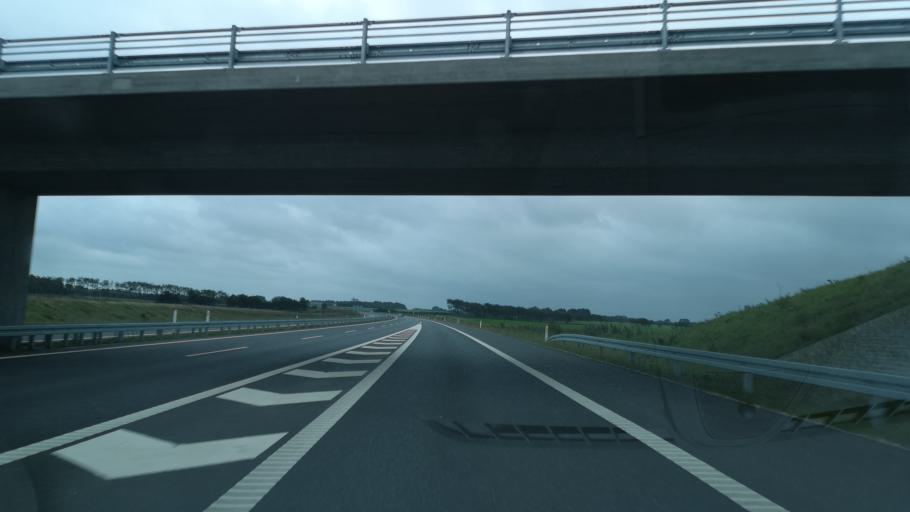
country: DK
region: Central Jutland
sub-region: Herning Kommune
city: Snejbjerg
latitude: 56.1481
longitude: 8.8706
